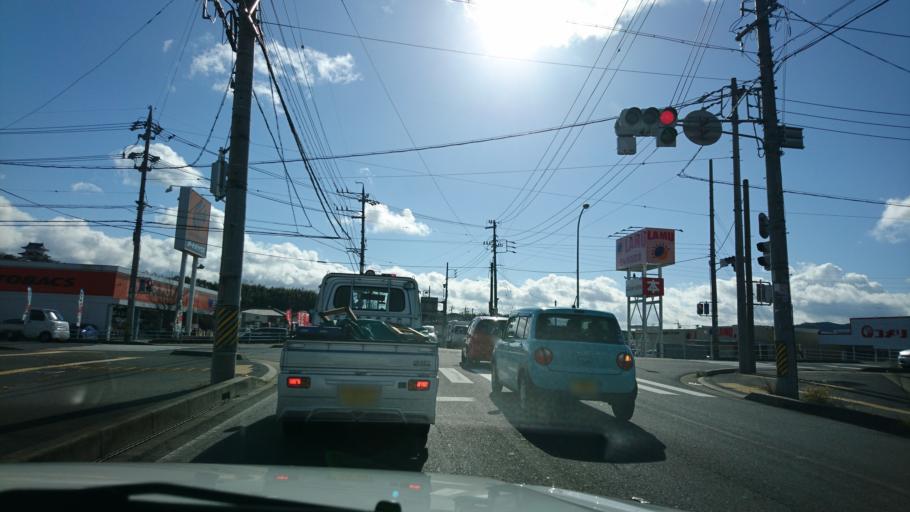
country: JP
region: Mie
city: Ueno-ebisumachi
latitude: 34.7752
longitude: 136.1238
